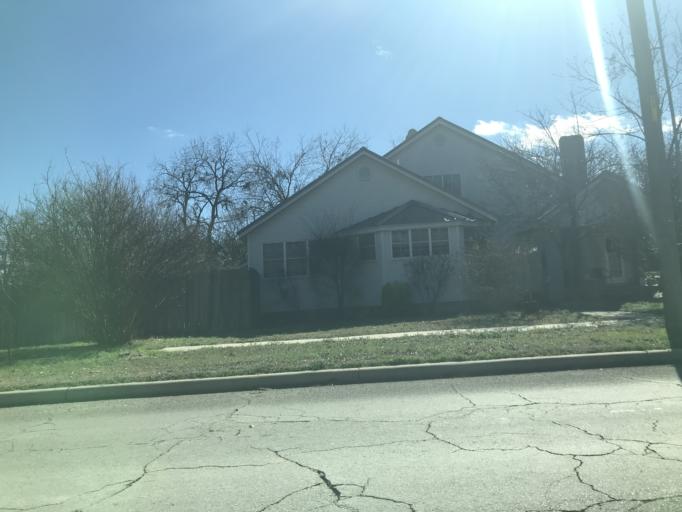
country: US
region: Texas
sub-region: Tom Green County
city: San Angelo
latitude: 31.4474
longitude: -100.4545
